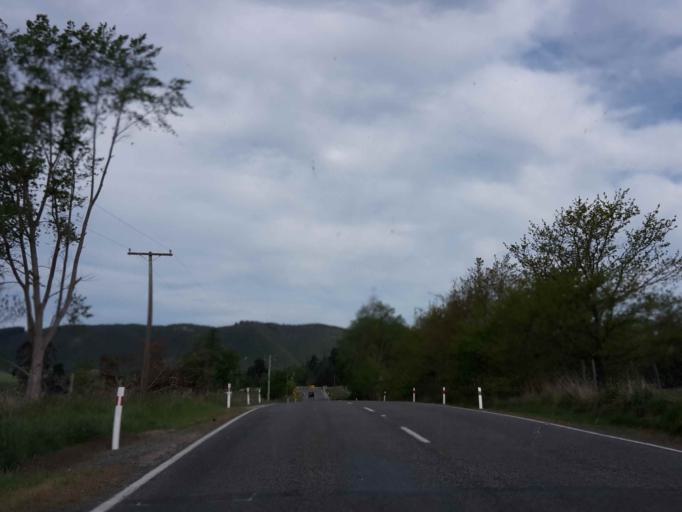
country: NZ
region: Canterbury
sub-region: Timaru District
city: Pleasant Point
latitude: -44.1168
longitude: 171.0219
